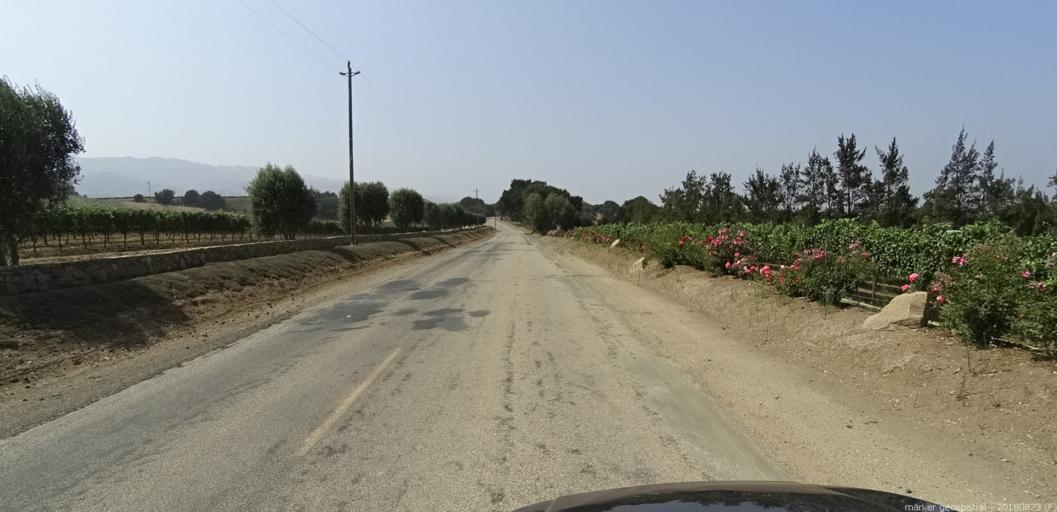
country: US
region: California
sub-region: Monterey County
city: Gonzales
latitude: 36.4616
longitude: -121.4526
